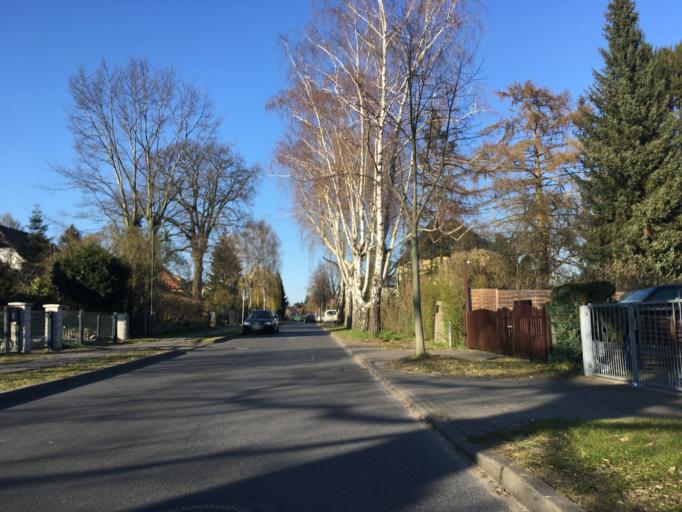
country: DE
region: Berlin
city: Buch
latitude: 52.6386
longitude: 13.5245
